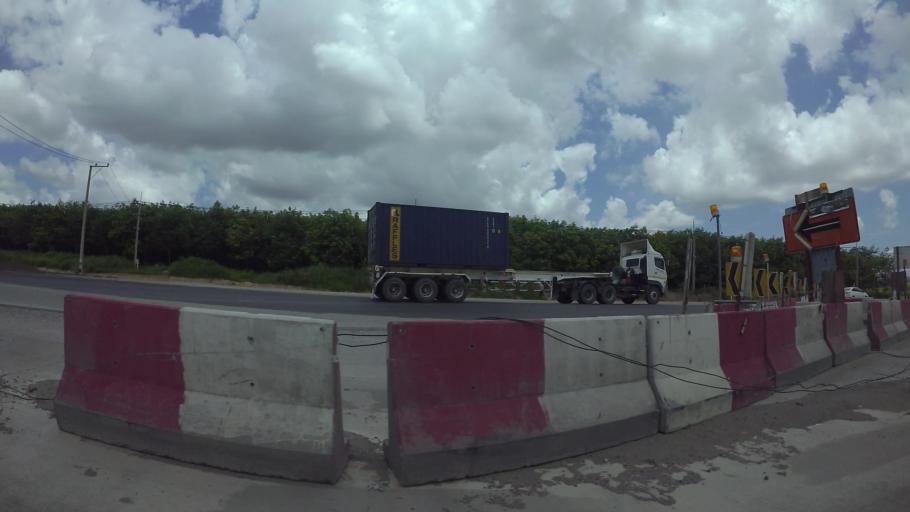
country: TH
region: Rayong
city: Nikhom Phattana
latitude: 12.8763
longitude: 101.0616
